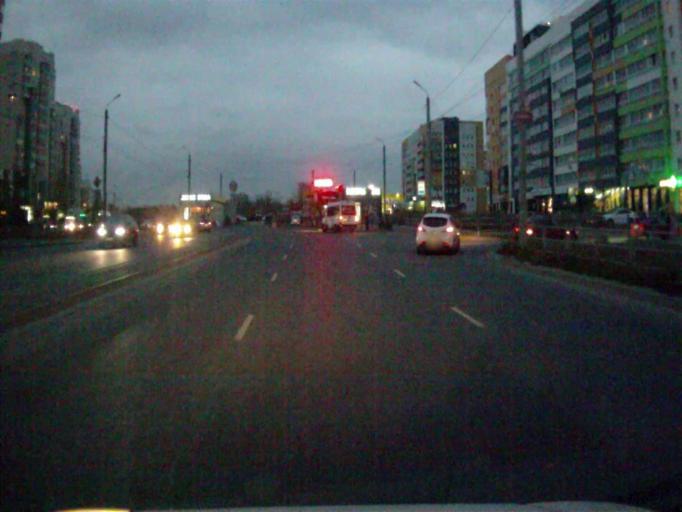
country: RU
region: Chelyabinsk
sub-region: Gorod Chelyabinsk
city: Chelyabinsk
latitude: 55.1629
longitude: 61.2949
